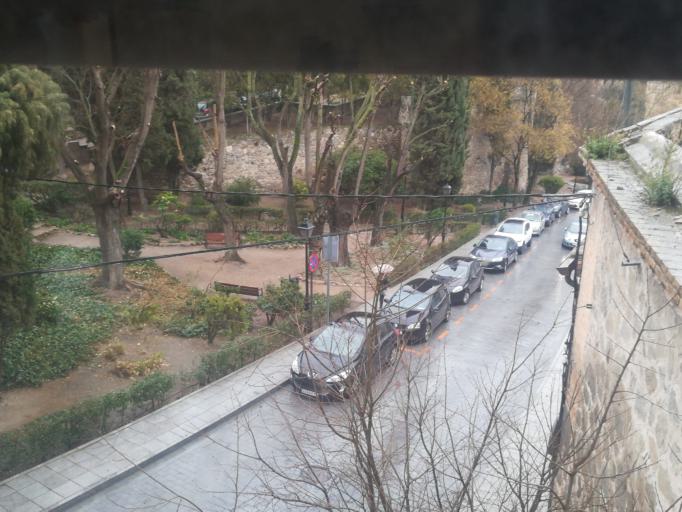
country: ES
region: Castille-La Mancha
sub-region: Province of Toledo
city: Toledo
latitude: 39.8587
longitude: -4.0334
